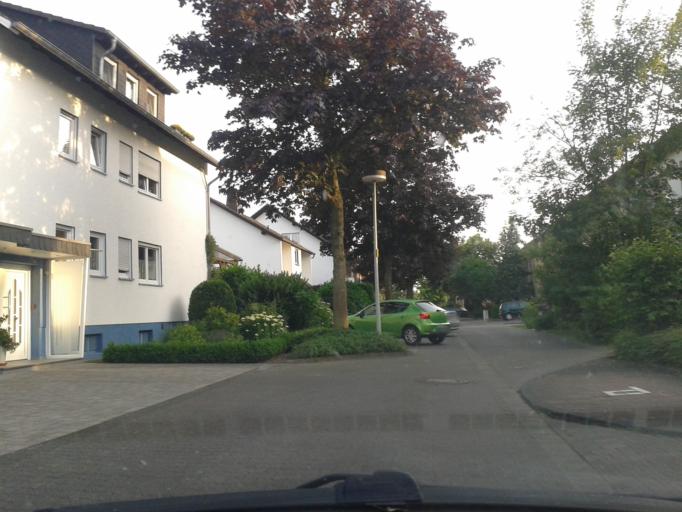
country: DE
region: North Rhine-Westphalia
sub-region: Regierungsbezirk Detmold
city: Paderborn
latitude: 51.7325
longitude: 8.6812
